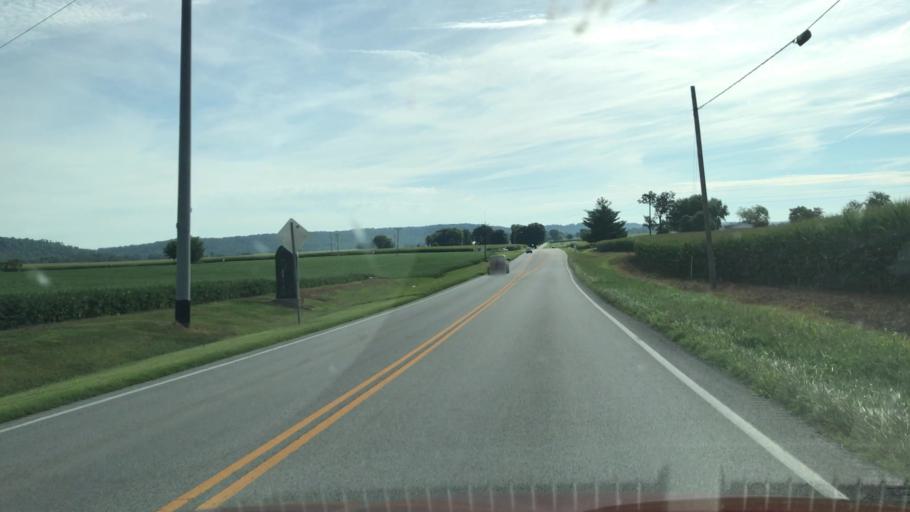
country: US
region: Kentucky
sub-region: Edmonson County
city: Brownsville
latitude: 37.0838
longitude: -86.2327
